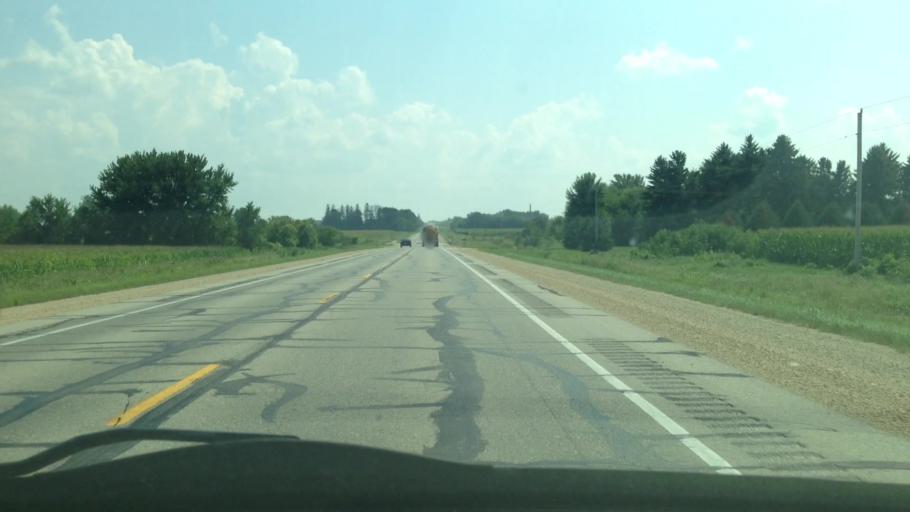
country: US
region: Iowa
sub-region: Chickasaw County
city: New Hampton
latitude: 43.2116
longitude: -92.2984
